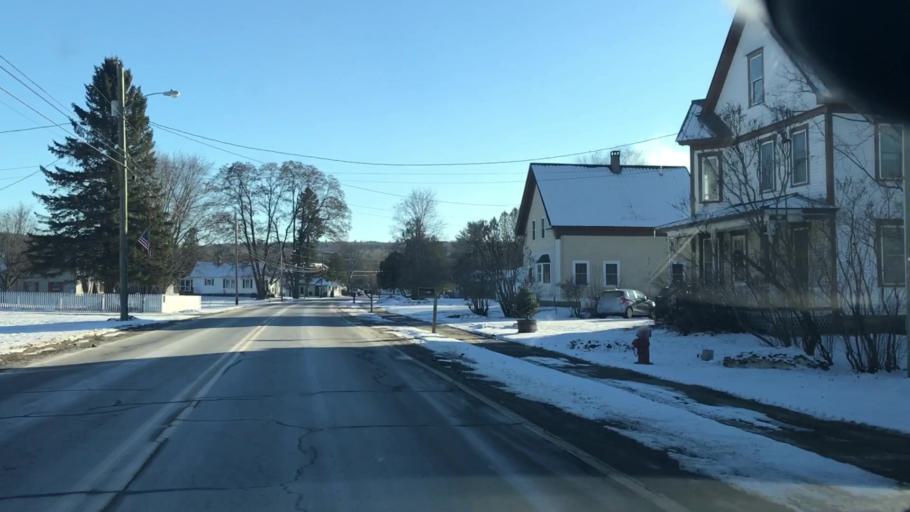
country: US
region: New Hampshire
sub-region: Grafton County
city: North Haverhill
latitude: 44.0861
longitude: -72.0254
